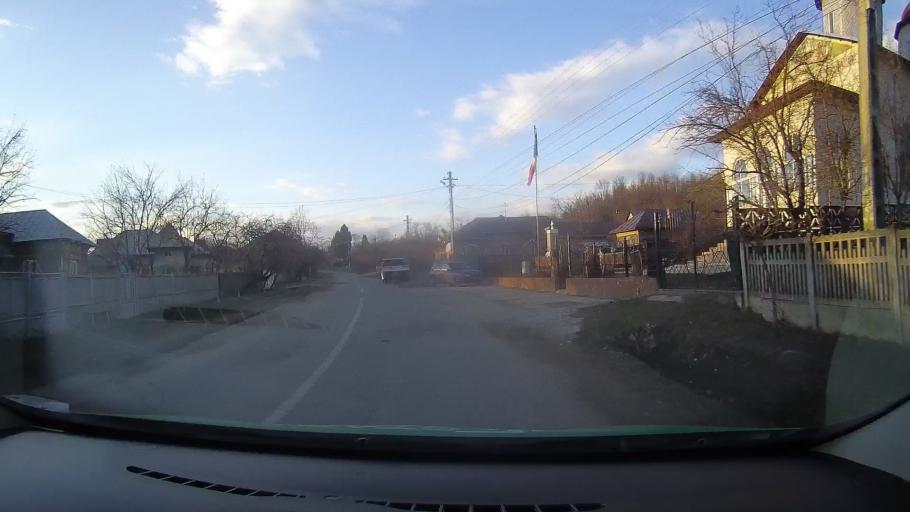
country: RO
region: Dambovita
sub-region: Comuna Gura Ocnitei
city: Adanca
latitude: 44.9189
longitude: 25.6163
